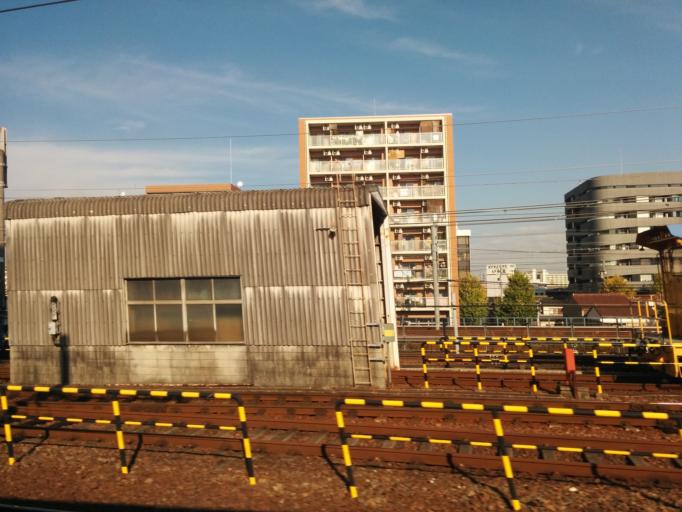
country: JP
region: Aichi
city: Nagoya-shi
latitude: 35.1824
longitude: 136.8737
